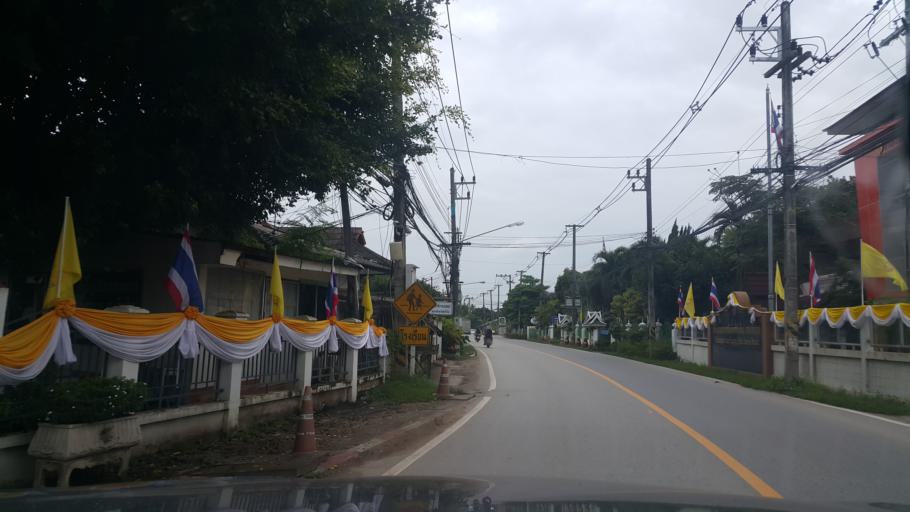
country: TH
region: Chiang Mai
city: San Sai
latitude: 18.8485
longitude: 99.0441
